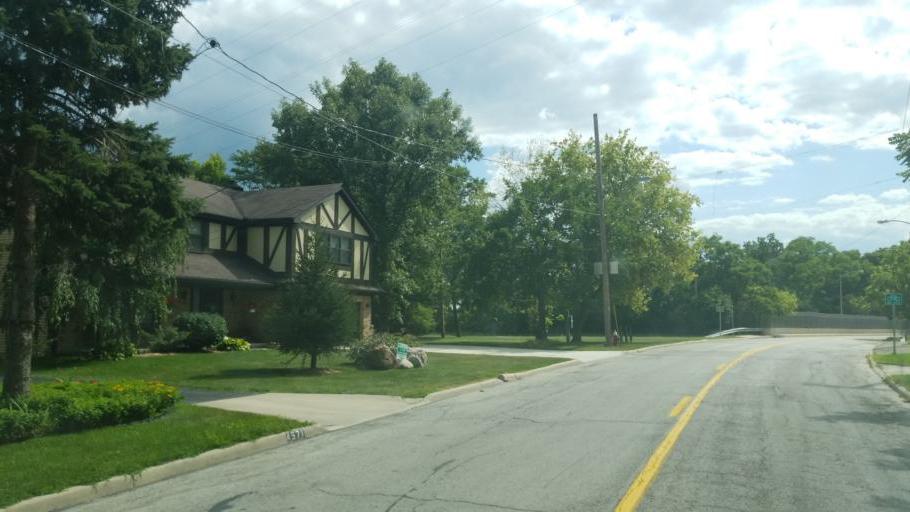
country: US
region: Ohio
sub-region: Wood County
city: Perrysburg
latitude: 41.5828
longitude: -83.6086
